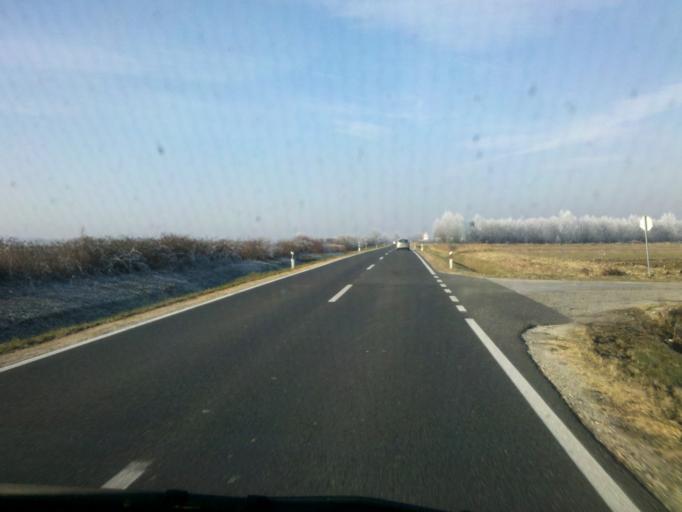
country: HR
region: Koprivnicko-Krizevacka
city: Kalinovac
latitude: 46.0048
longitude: 17.1091
